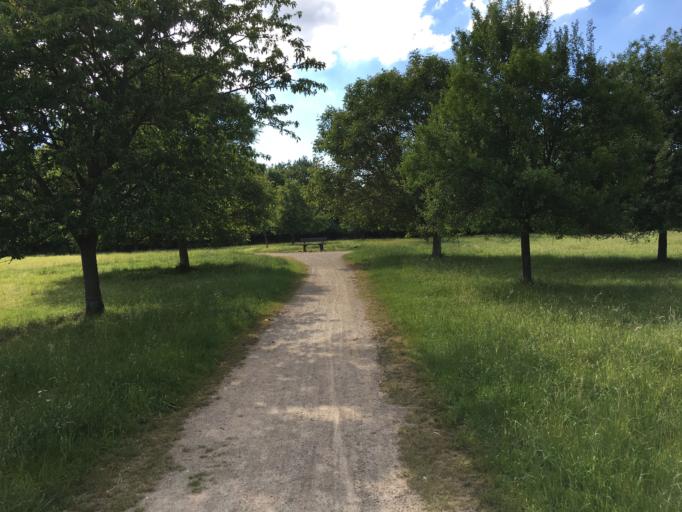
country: DE
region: North Rhine-Westphalia
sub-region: Regierungsbezirk Koln
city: Dueren
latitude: 50.7852
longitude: 6.4731
